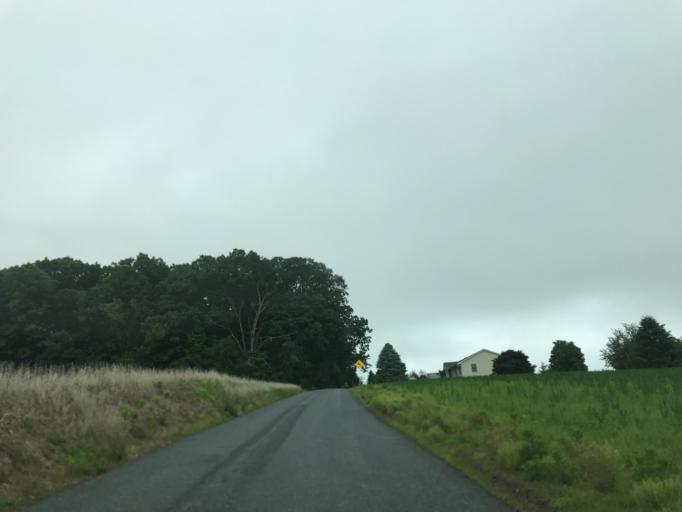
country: US
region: Pennsylvania
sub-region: York County
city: Stewartstown
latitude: 39.7070
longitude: -76.5092
